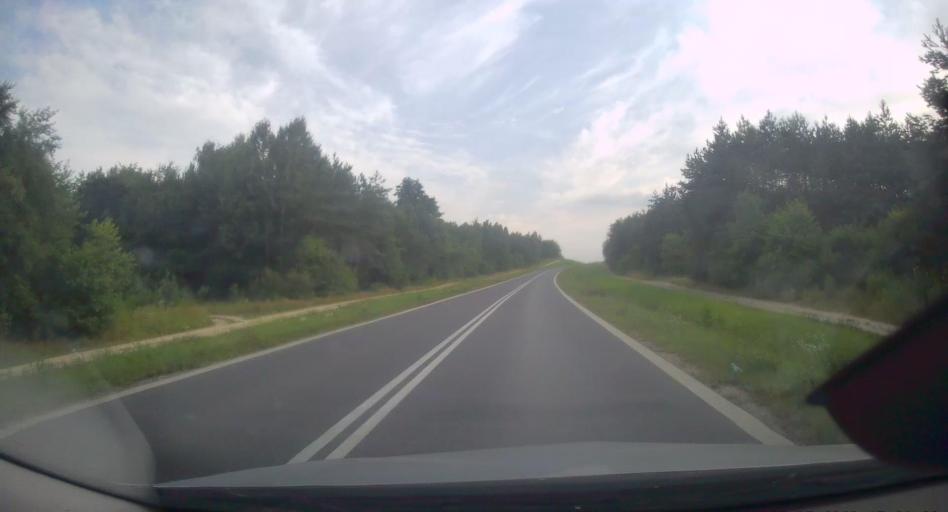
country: PL
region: Lesser Poland Voivodeship
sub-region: Powiat brzeski
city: Brzesko
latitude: 50.0133
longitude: 20.6184
